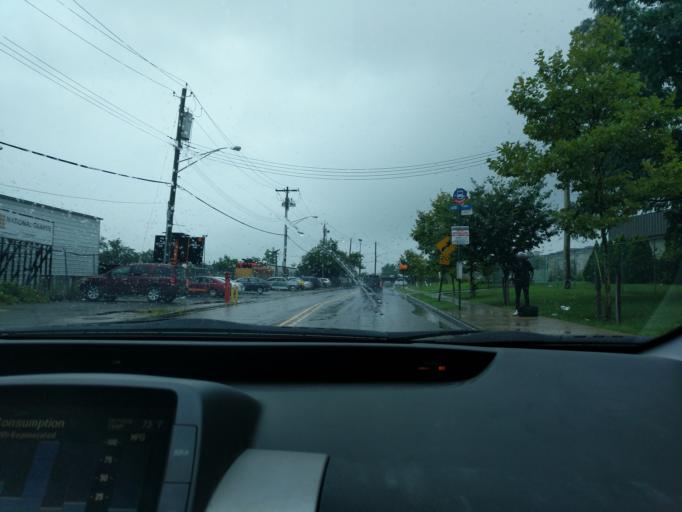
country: US
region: New Jersey
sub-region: Hudson County
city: Bayonne
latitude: 40.6391
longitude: -74.1420
